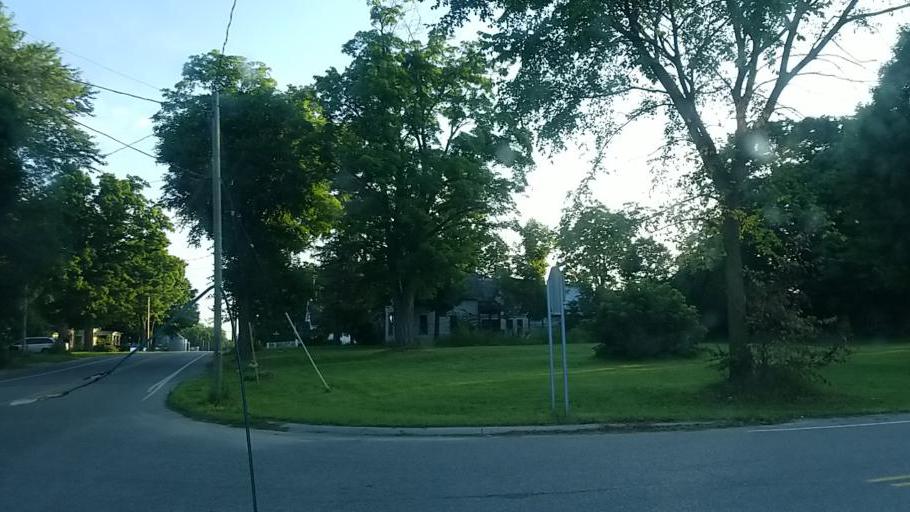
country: US
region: Michigan
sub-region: Montcalm County
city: Howard City
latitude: 43.3594
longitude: -85.4029
